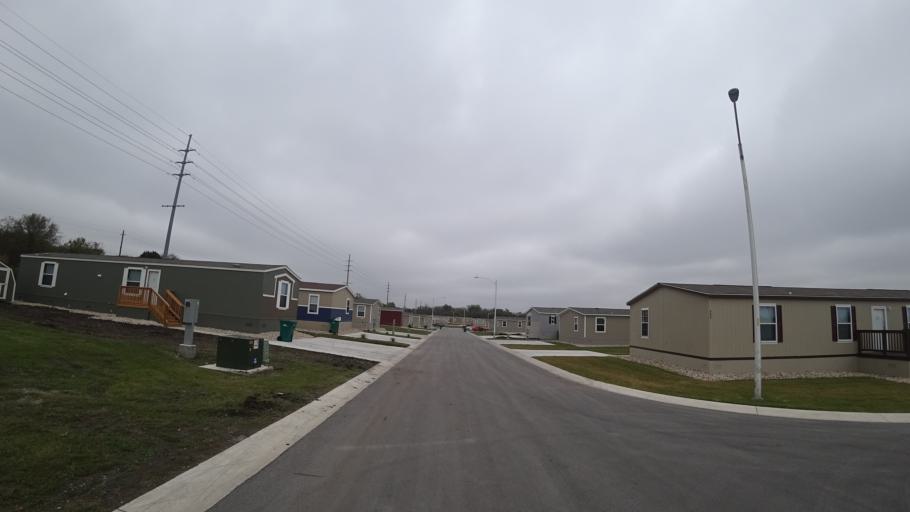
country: US
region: Texas
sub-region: Travis County
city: Pflugerville
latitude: 30.3906
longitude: -97.6386
